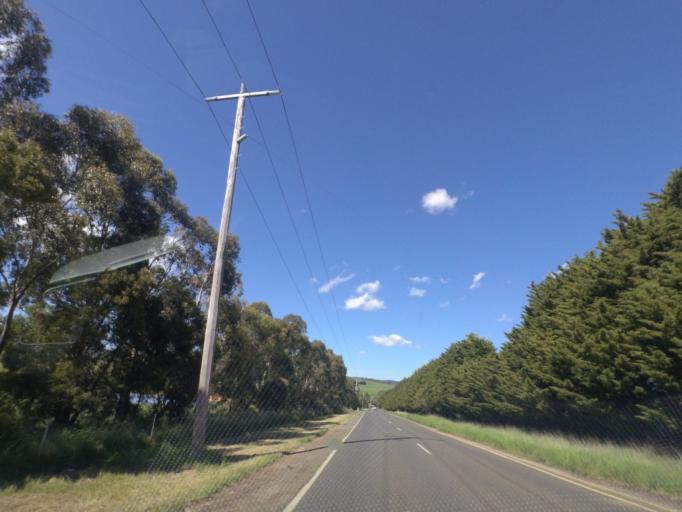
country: AU
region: Victoria
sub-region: Moorabool
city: Bacchus Marsh
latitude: -37.5649
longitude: 144.2608
